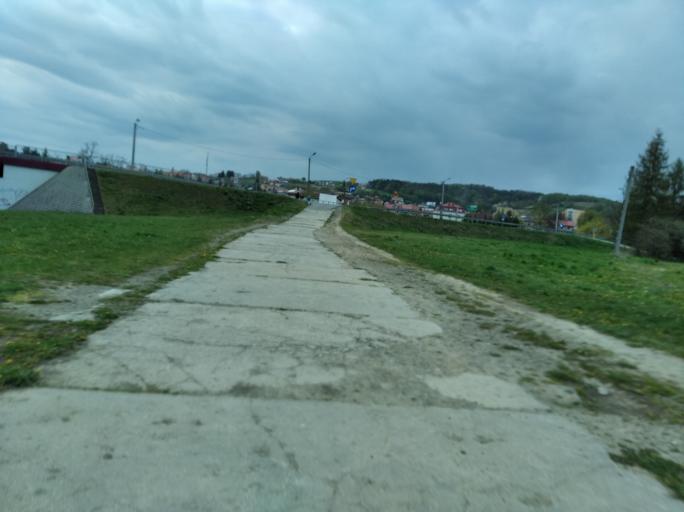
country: PL
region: Subcarpathian Voivodeship
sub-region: Powiat strzyzowski
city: Strzyzow
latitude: 49.8672
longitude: 21.7936
